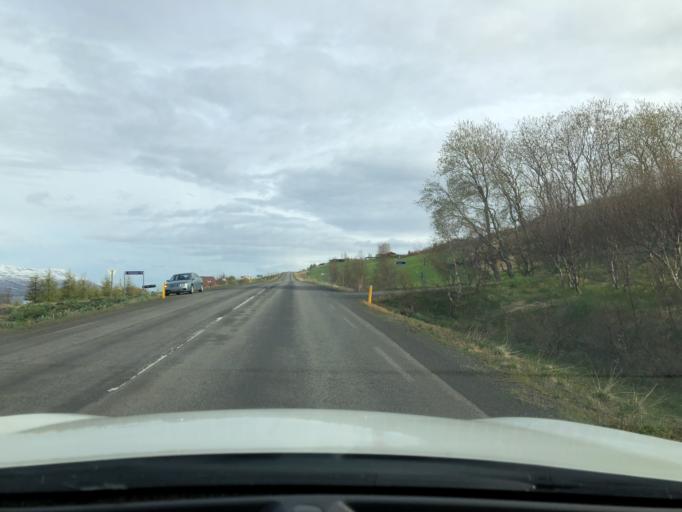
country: IS
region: Northeast
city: Akureyri
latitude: 65.7032
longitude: -18.0636
